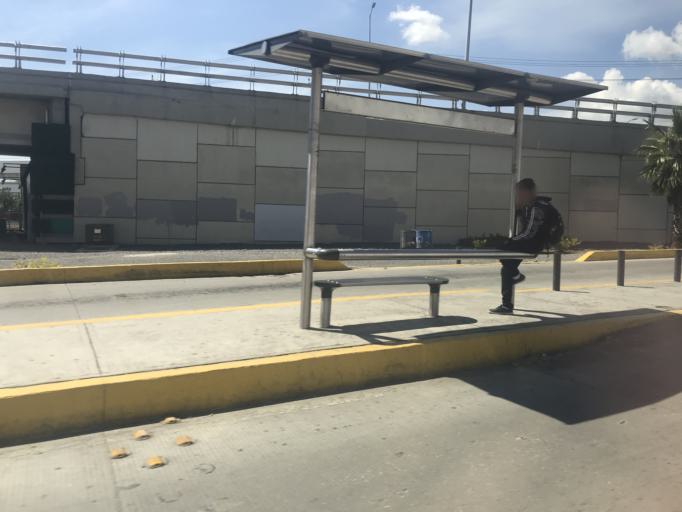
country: MX
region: Puebla
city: Cholula
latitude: 19.0607
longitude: -98.2954
